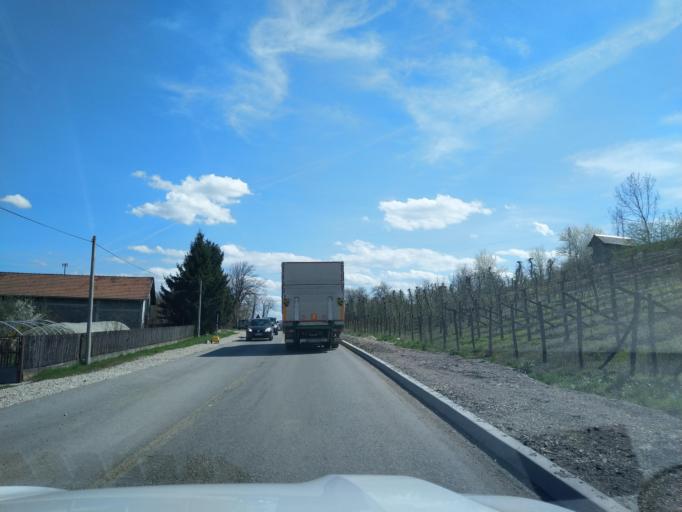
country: RS
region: Central Serbia
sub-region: Zlatiborski Okrug
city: Pozega
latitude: 43.8238
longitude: 20.0814
